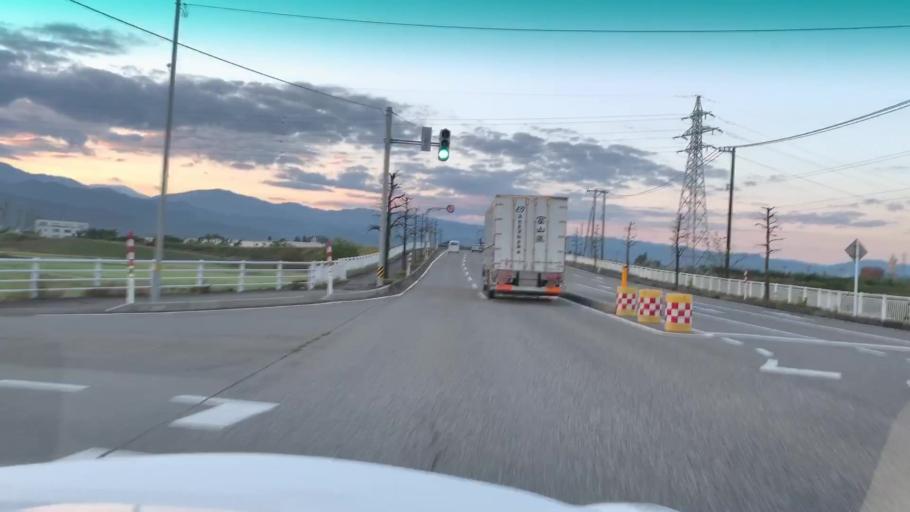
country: JP
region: Toyama
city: Kamiichi
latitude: 36.6960
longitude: 137.3428
